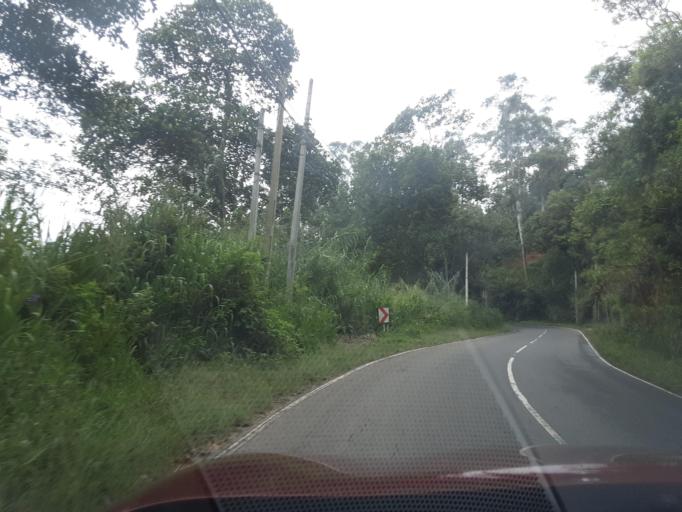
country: LK
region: Uva
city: Haputale
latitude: 6.8570
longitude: 80.9654
